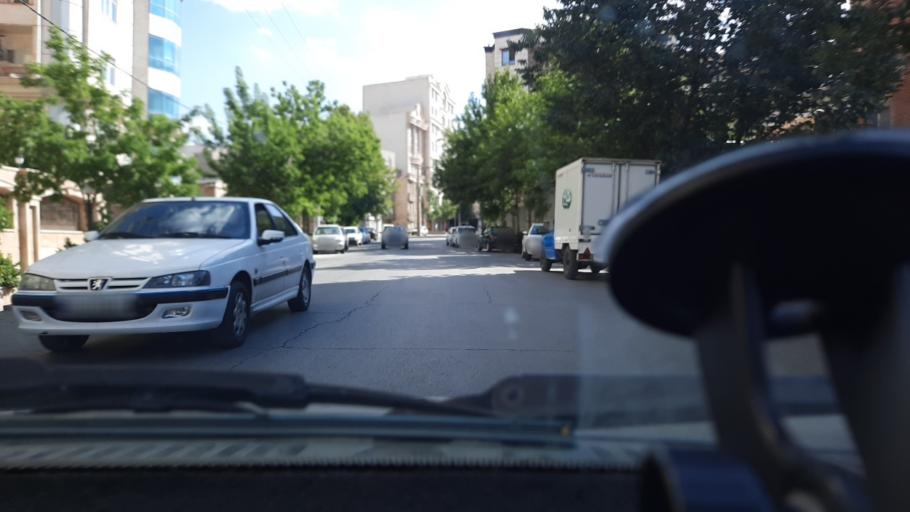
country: IR
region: Markazi
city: Arak
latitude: 34.0790
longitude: 49.6879
